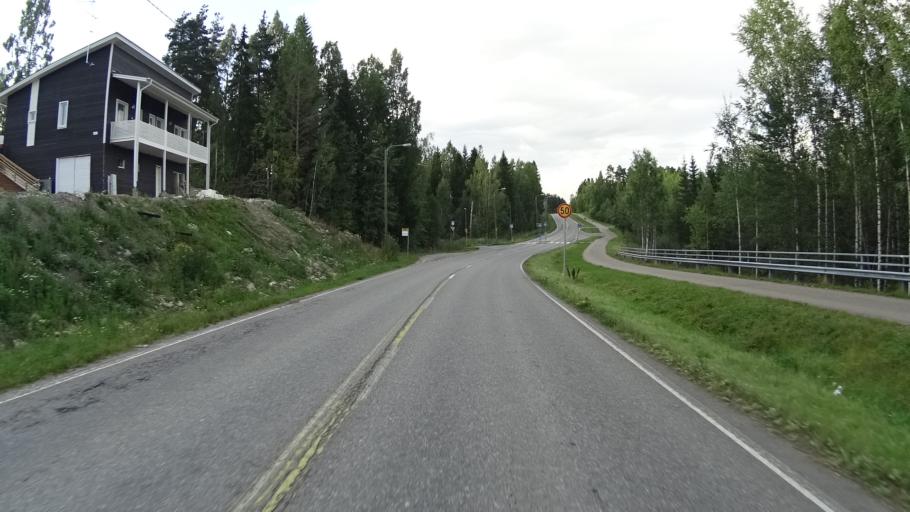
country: FI
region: Uusimaa
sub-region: Helsinki
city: Kilo
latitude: 60.3323
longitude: 24.8627
